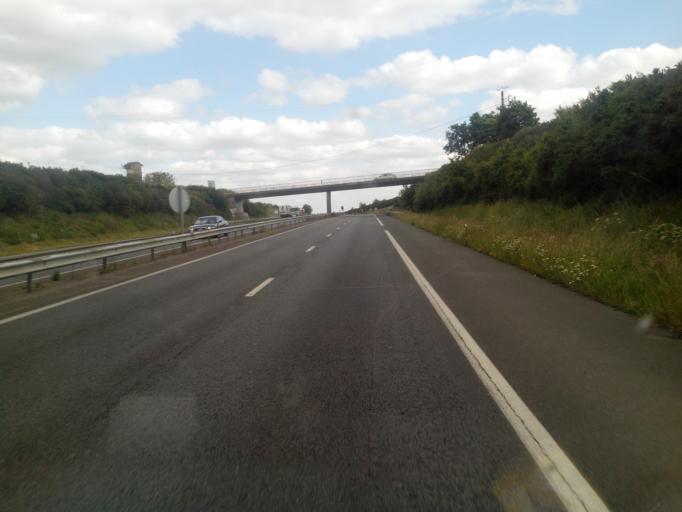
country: FR
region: Brittany
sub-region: Departement des Cotes-d'Armor
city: Plenee-Jugon
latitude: 48.3930
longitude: -2.3980
